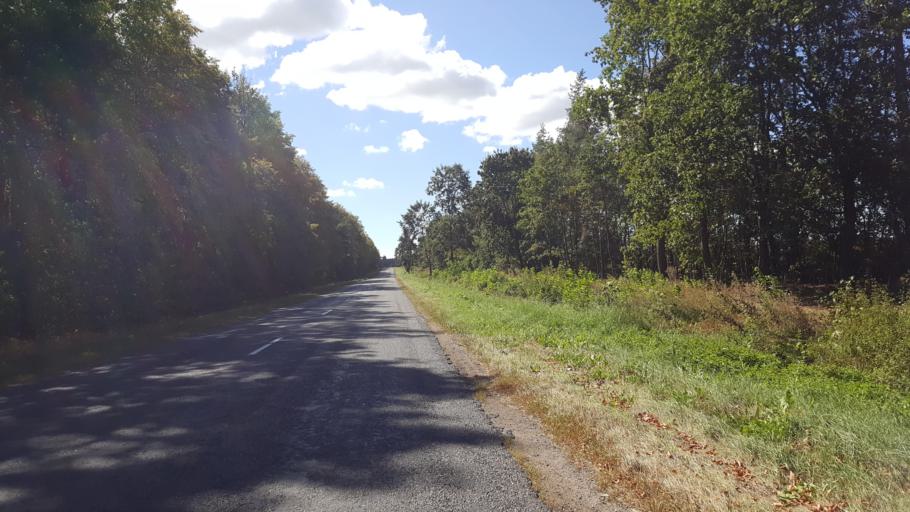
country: BY
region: Brest
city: Vysokaye
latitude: 52.3308
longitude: 23.3279
